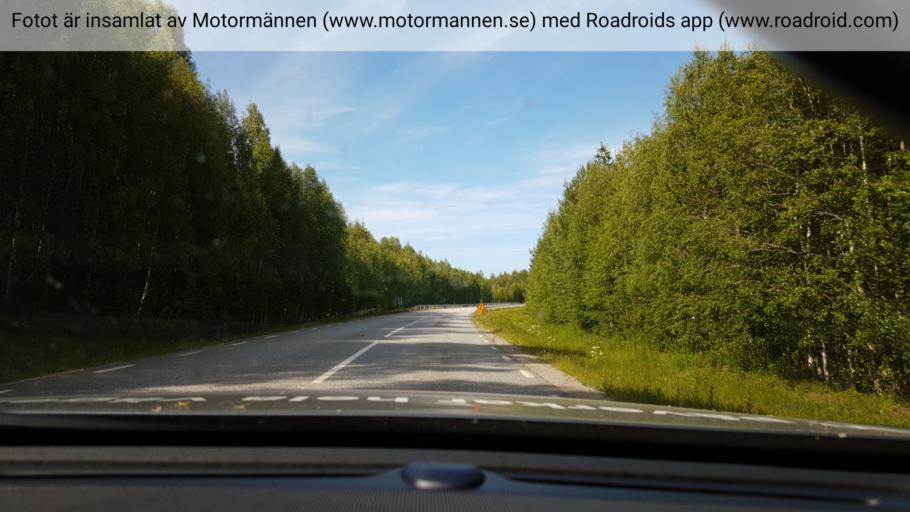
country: SE
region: Vaesterbotten
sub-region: Dorotea Kommun
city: Dorotea
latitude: 64.2493
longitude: 16.6295
